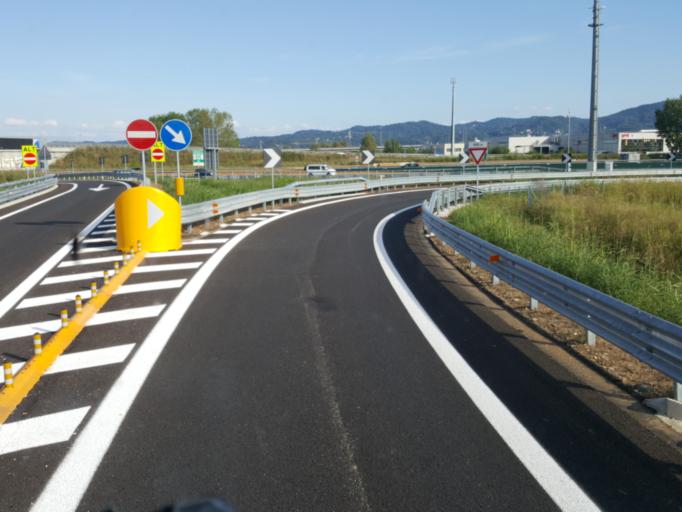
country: IT
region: Piedmont
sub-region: Provincia di Torino
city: Settimo Torinese
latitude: 45.1362
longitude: 7.7343
